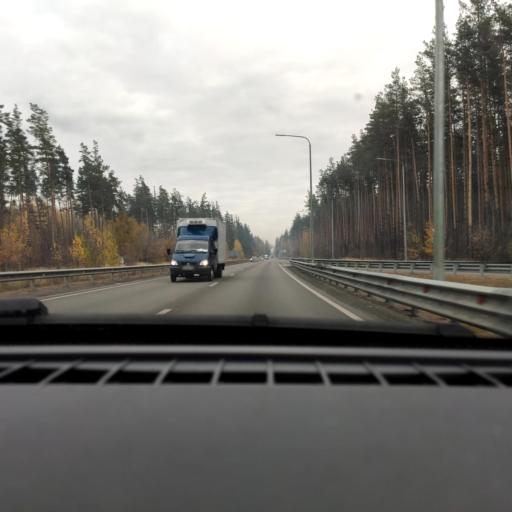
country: RU
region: Voronezj
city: Somovo
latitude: 51.6933
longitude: 39.3063
